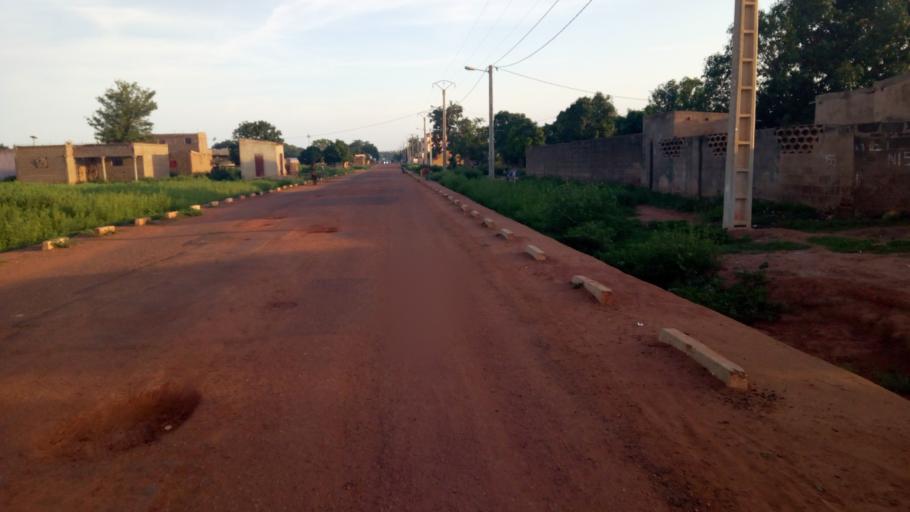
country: ML
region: Sikasso
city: Koutiala
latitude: 12.4099
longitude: -5.4452
